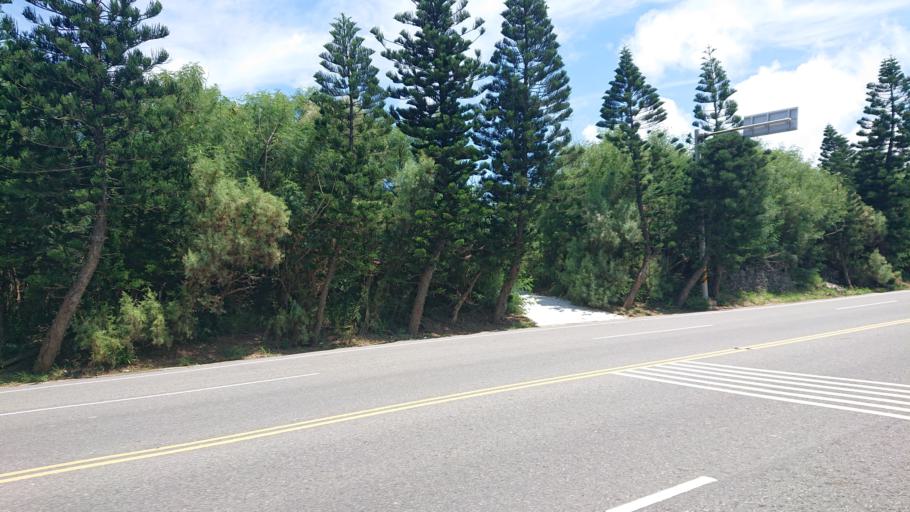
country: TW
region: Taiwan
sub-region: Penghu
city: Ma-kung
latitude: 23.6593
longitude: 119.5560
